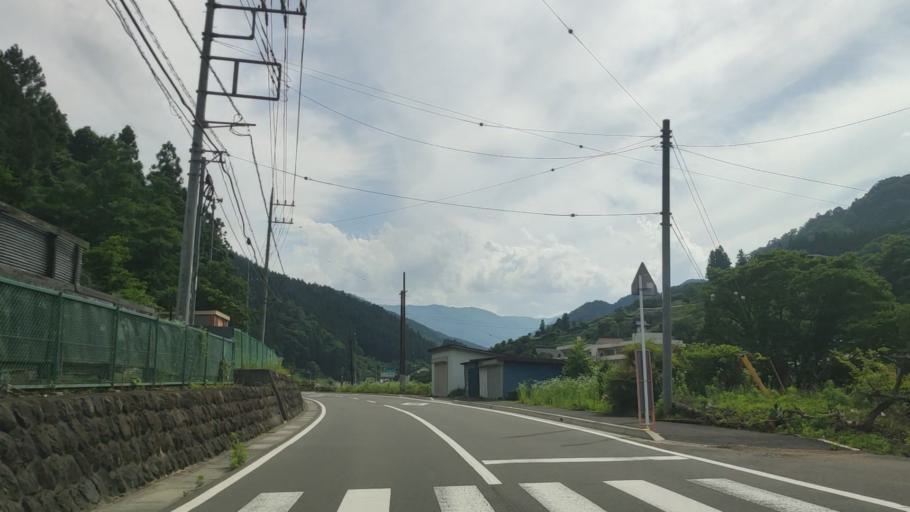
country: JP
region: Gunma
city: Tomioka
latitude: 36.1756
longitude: 138.7376
